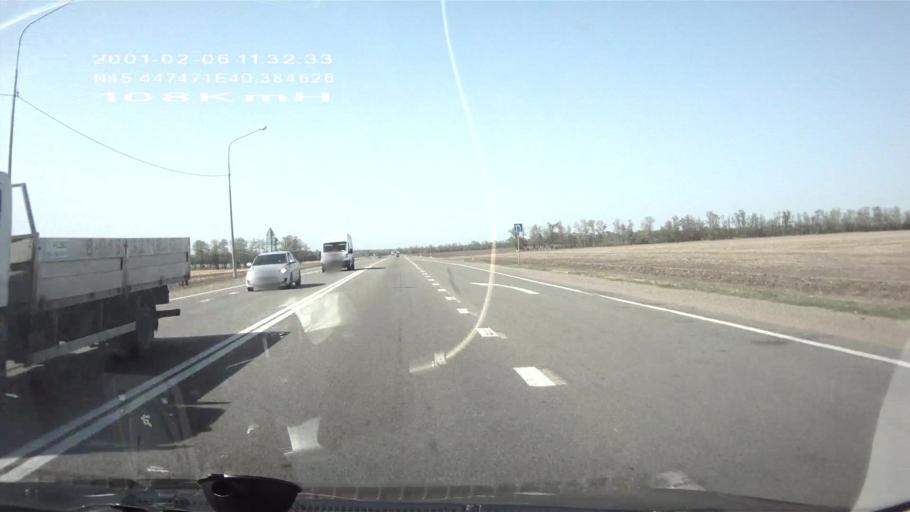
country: RU
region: Krasnodarskiy
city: Kazanskaya
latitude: 45.4471
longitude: 40.3853
